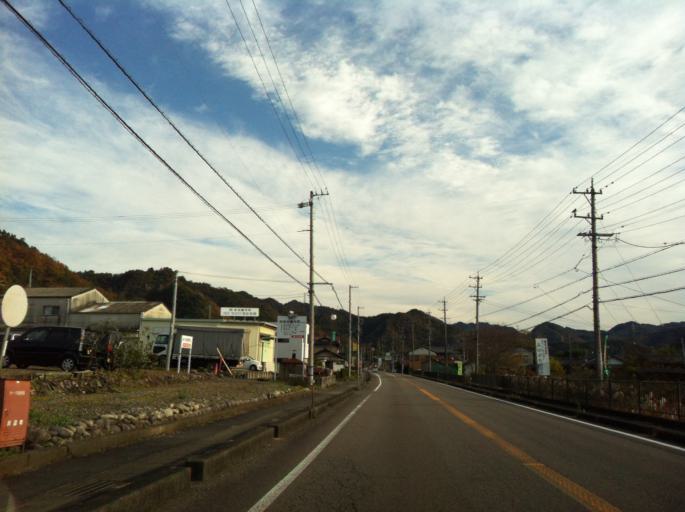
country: JP
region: Gifu
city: Minokamo
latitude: 35.5122
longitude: 137.0856
